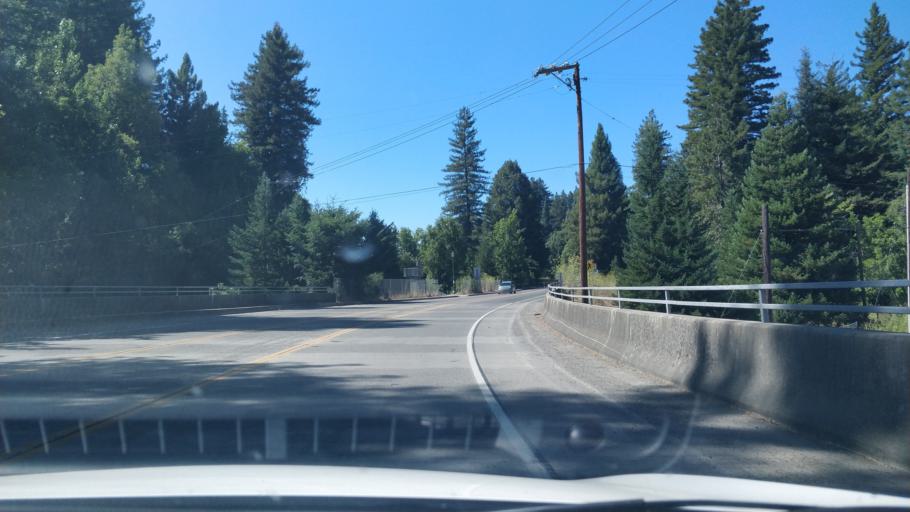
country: US
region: California
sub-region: Sonoma County
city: Guerneville
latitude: 38.4991
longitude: -122.9933
